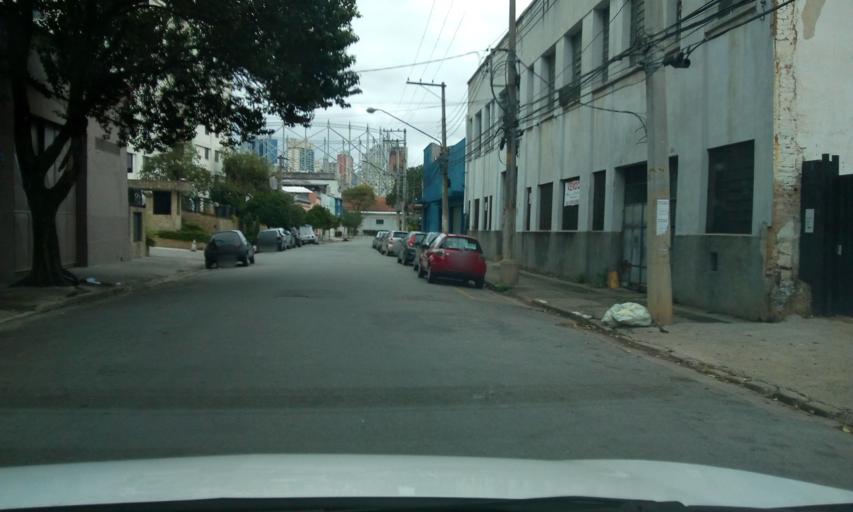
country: BR
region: Sao Paulo
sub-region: Sao Paulo
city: Sao Paulo
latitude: -23.5482
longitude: -46.6233
